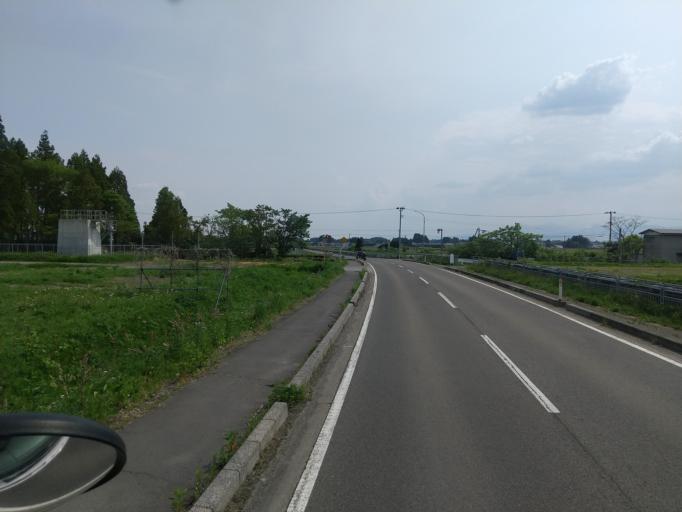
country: JP
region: Iwate
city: Hanamaki
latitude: 39.3909
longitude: 141.0878
